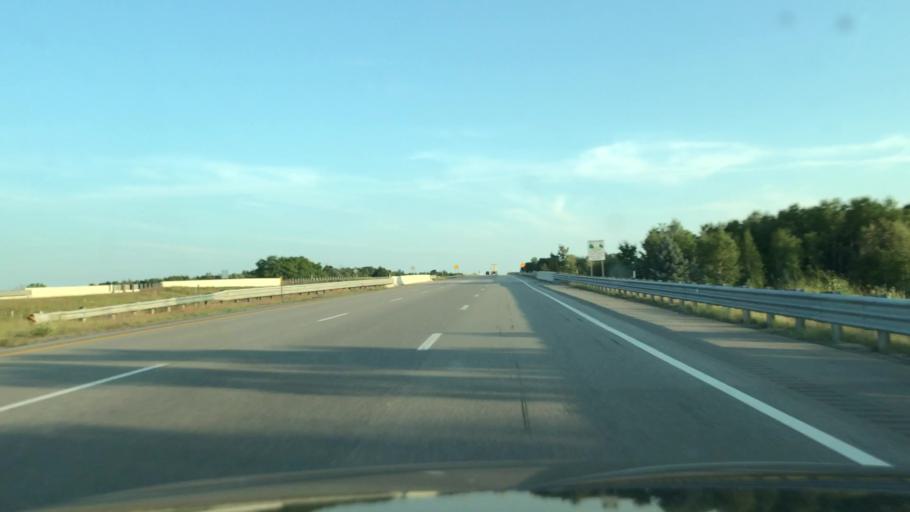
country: US
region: Michigan
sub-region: Osceola County
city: Reed City
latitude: 43.8884
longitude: -85.5282
